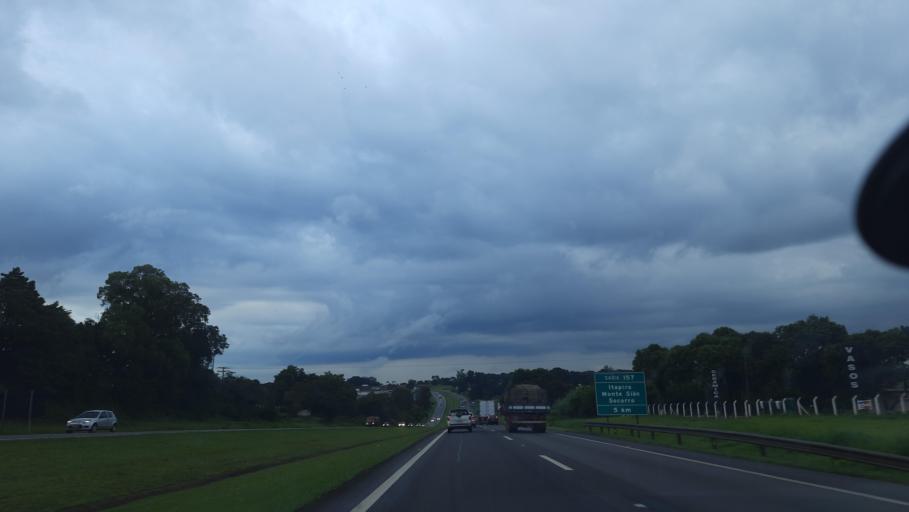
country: BR
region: Sao Paulo
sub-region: Mogi-Mirim
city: Mogi Mirim
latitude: -22.4271
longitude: -46.9827
